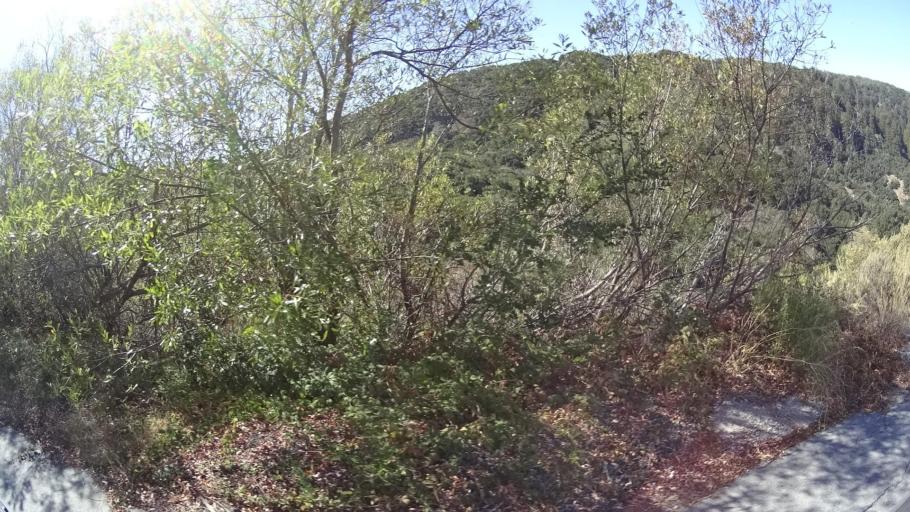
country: US
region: California
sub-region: Monterey County
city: Carmel Valley Village
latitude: 36.4772
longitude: -121.8007
